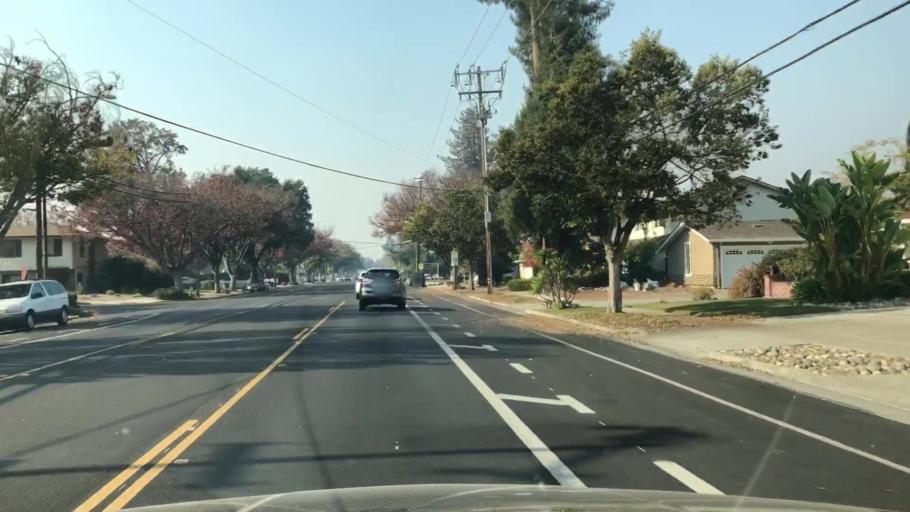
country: US
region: California
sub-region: Santa Clara County
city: Campbell
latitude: 37.3031
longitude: -121.9833
